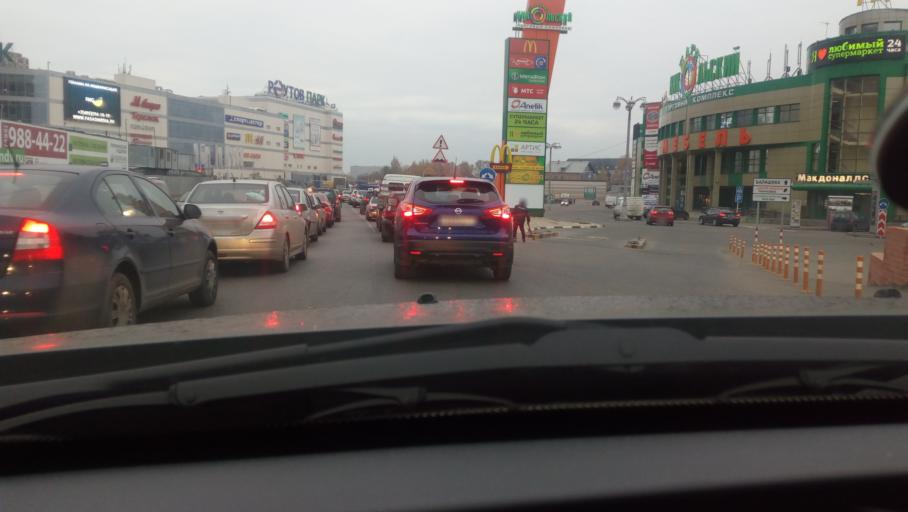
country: RU
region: Moskovskaya
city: Reutov
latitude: 55.7498
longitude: 37.8855
